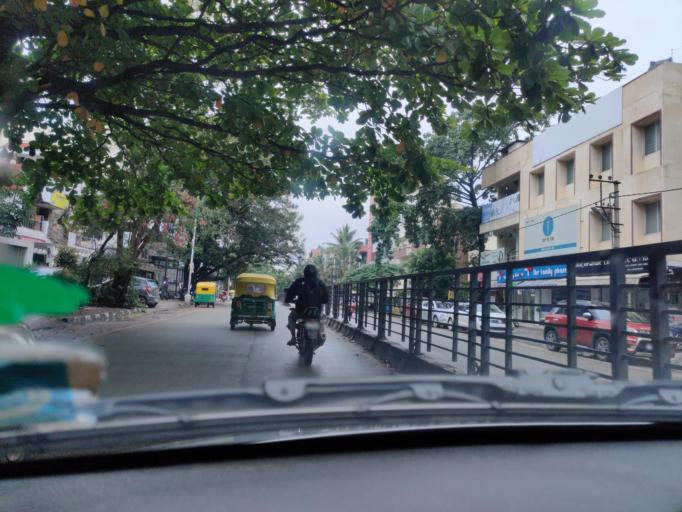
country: IN
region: Karnataka
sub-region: Bangalore Urban
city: Bangalore
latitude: 13.0198
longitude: 77.6432
